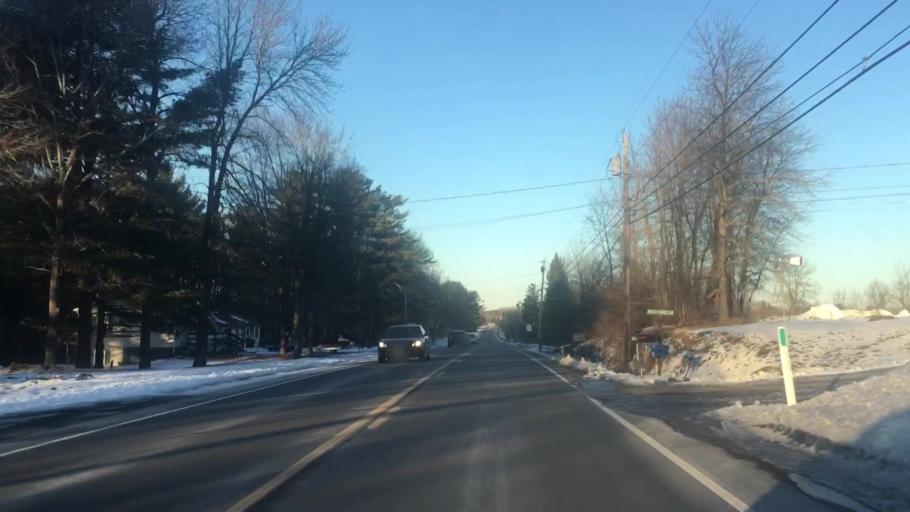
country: US
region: Maine
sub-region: Kennebec County
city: Benton
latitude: 44.5877
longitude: -69.5448
